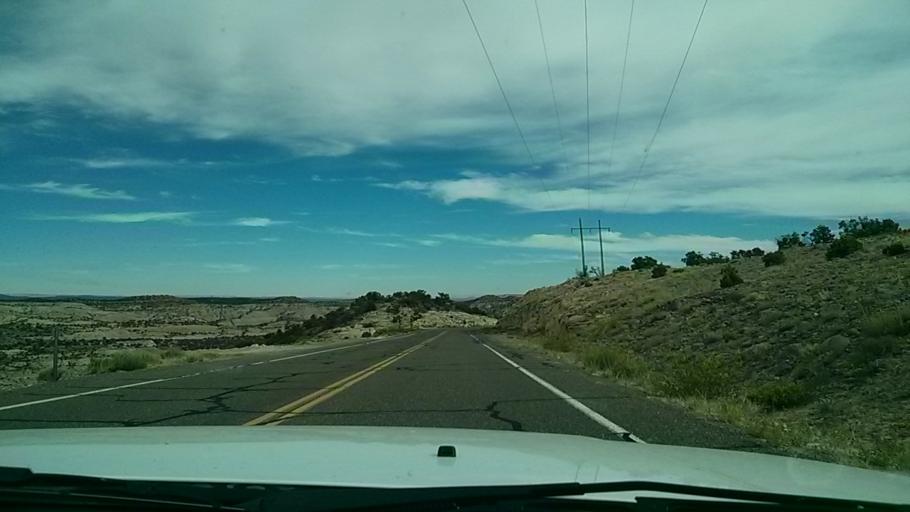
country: US
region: Utah
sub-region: Wayne County
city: Loa
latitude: 37.8355
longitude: -111.4180
